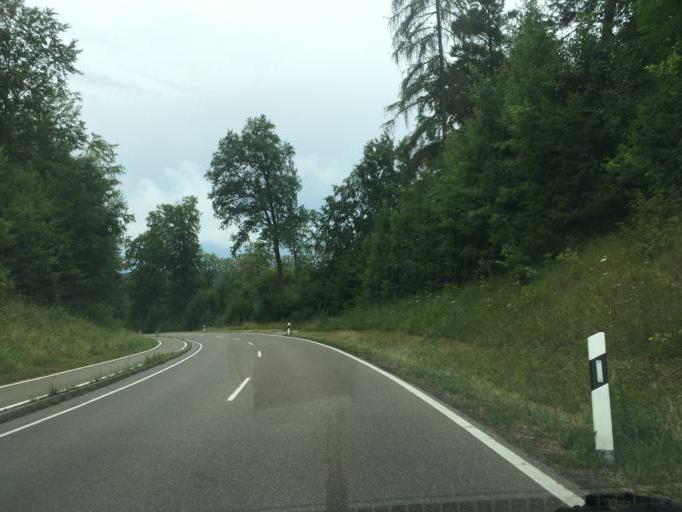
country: DE
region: Baden-Wuerttemberg
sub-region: Tuebingen Region
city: Dettenhausen
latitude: 48.5945
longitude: 9.1063
